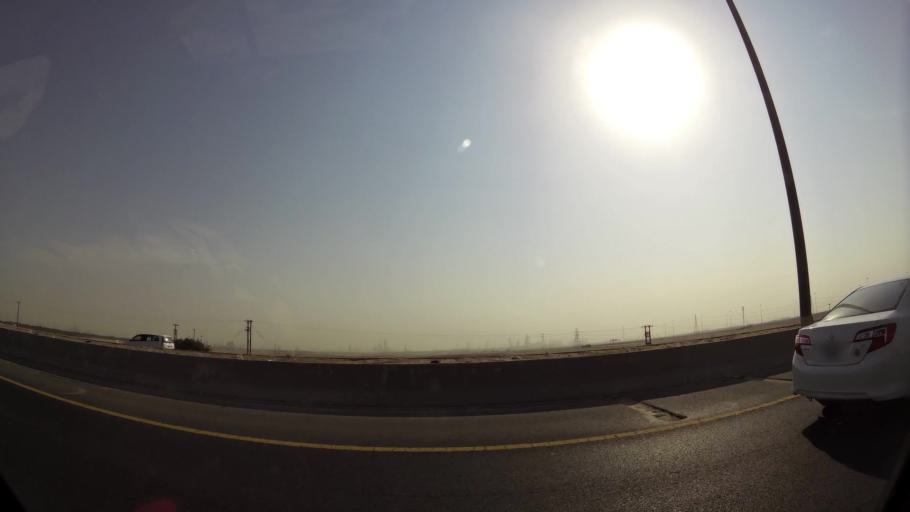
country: KW
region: Al Ahmadi
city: Al Ahmadi
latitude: 29.0396
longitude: 48.0934
